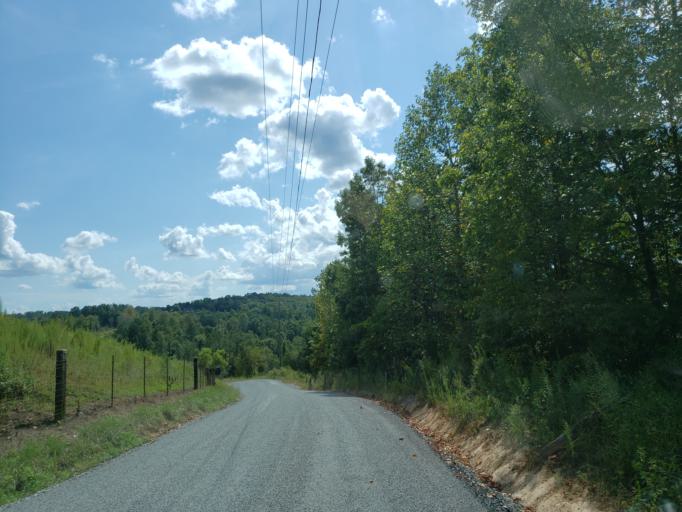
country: US
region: Georgia
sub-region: Pickens County
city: Jasper
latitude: 34.4236
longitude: -84.4565
